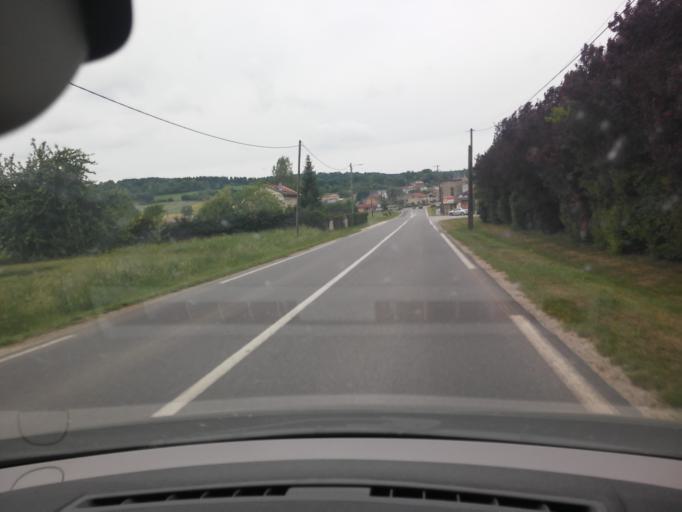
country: FR
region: Lorraine
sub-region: Departement de la Meuse
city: Lerouville
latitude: 48.8189
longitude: 5.5139
